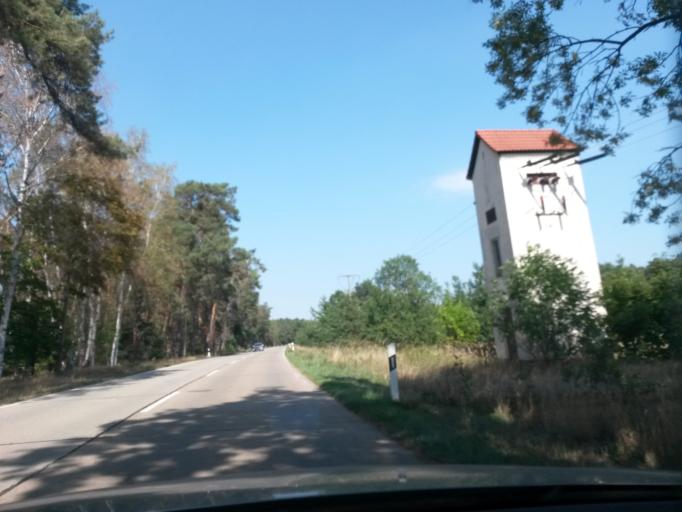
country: DE
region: Saxony-Anhalt
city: Jerichow
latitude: 52.4710
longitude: 12.0235
